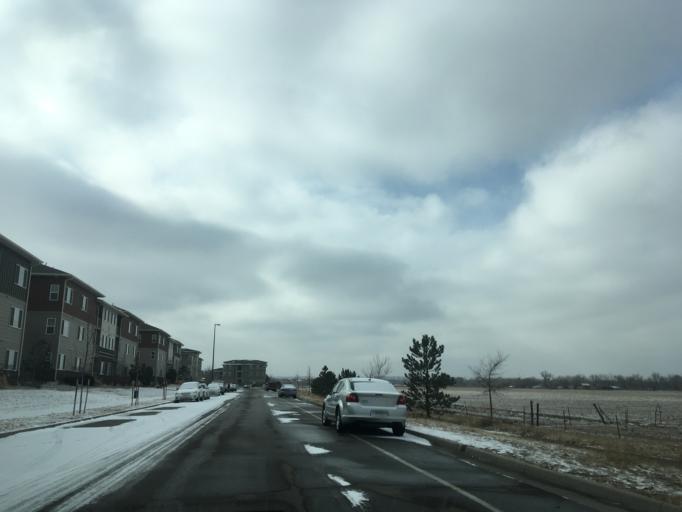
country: US
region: Colorado
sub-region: Boulder County
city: Lafayette
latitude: 39.9758
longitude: -105.0827
